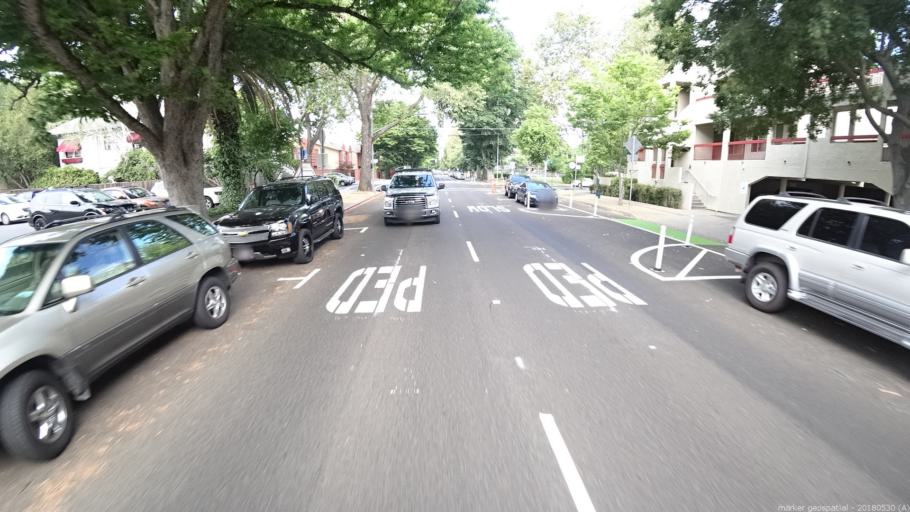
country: US
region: California
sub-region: Sacramento County
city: Sacramento
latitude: 38.5724
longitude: -121.4964
